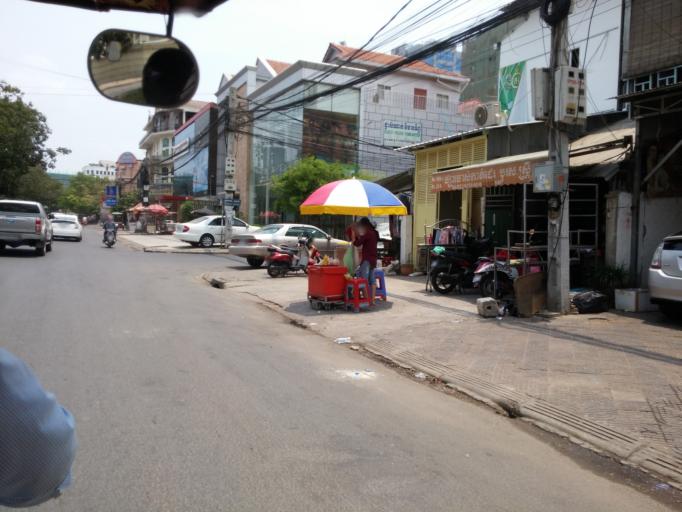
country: KH
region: Phnom Penh
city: Phnom Penh
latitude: 11.5598
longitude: 104.9174
